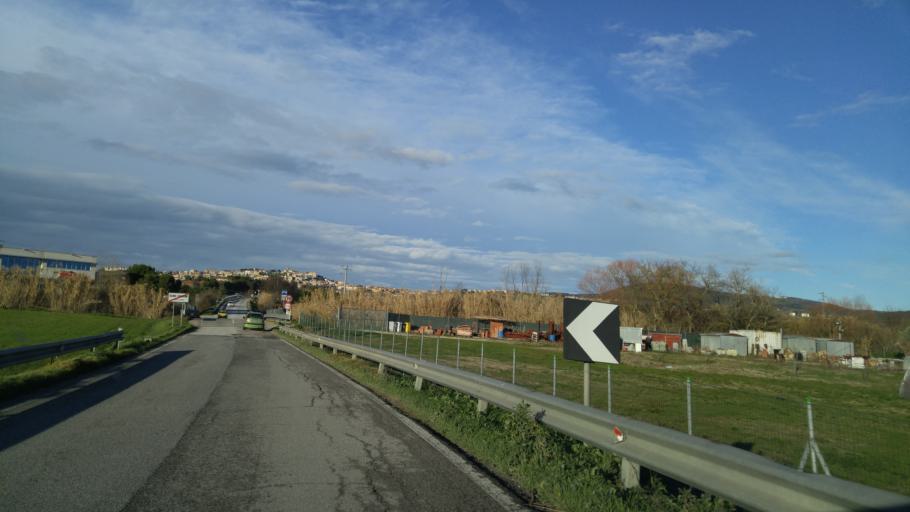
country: IT
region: The Marches
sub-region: Provincia di Ancona
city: Camerano
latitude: 43.5025
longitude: 13.5458
